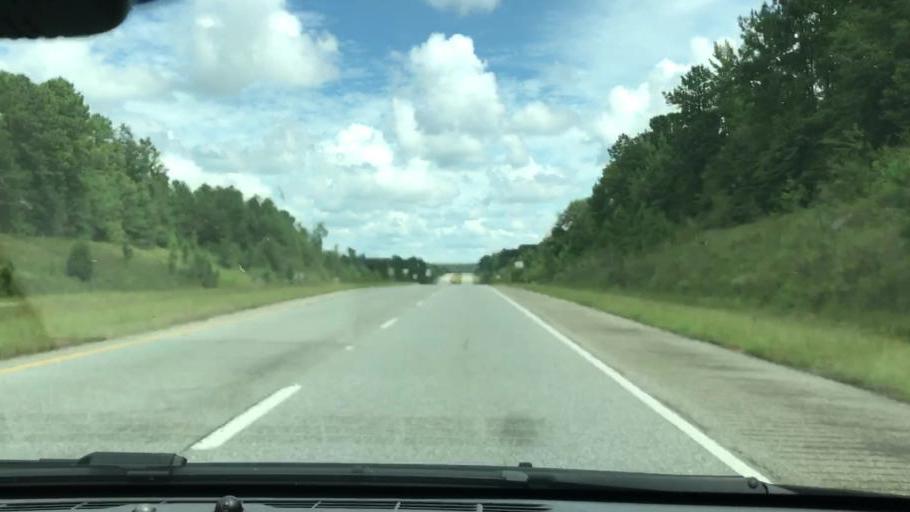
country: US
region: Georgia
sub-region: Stewart County
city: Lumpkin
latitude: 32.1660
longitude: -84.8297
